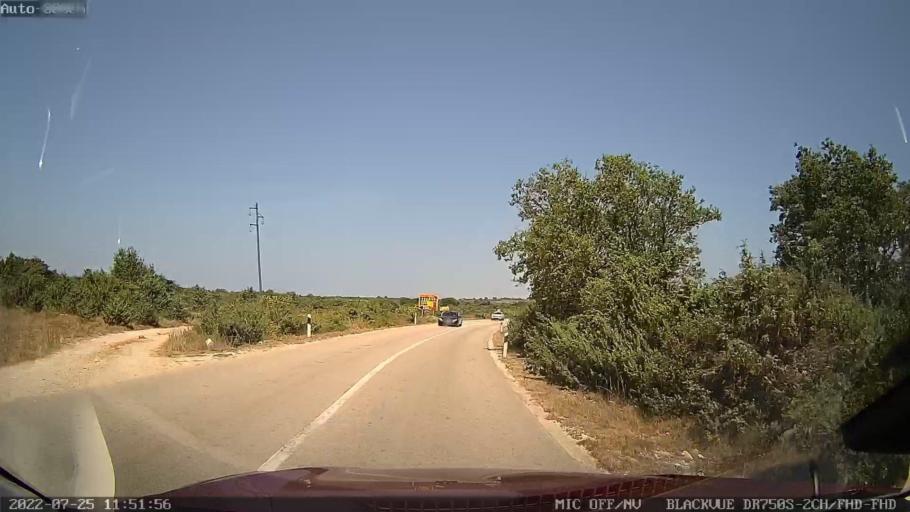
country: HR
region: Zadarska
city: Vrsi
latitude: 44.2432
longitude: 15.2481
